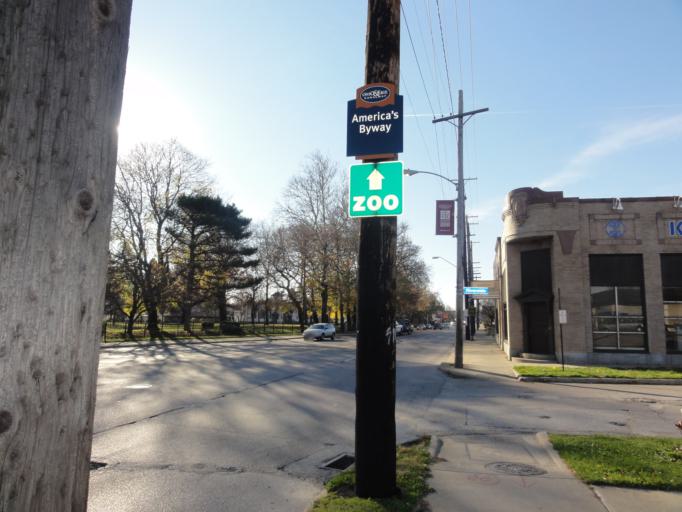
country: US
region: Ohio
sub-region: Cuyahoga County
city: Cleveland
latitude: 41.4683
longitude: -81.7001
